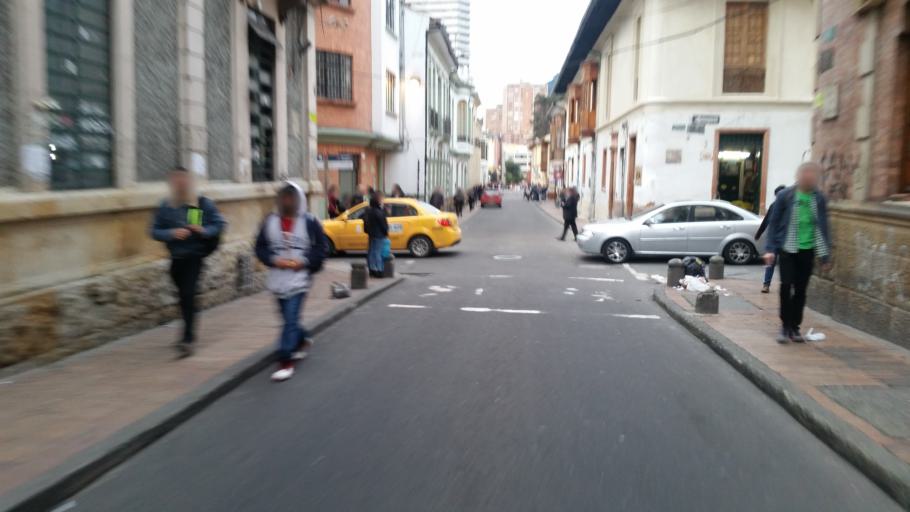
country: CO
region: Bogota D.C.
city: Bogota
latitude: 4.5987
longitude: -74.0727
